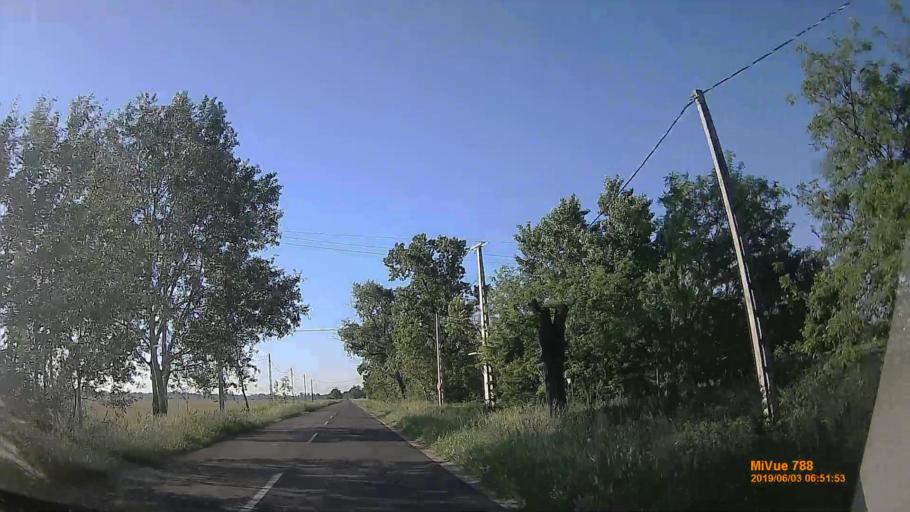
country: HU
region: Pest
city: Bugyi
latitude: 47.2069
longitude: 19.1902
